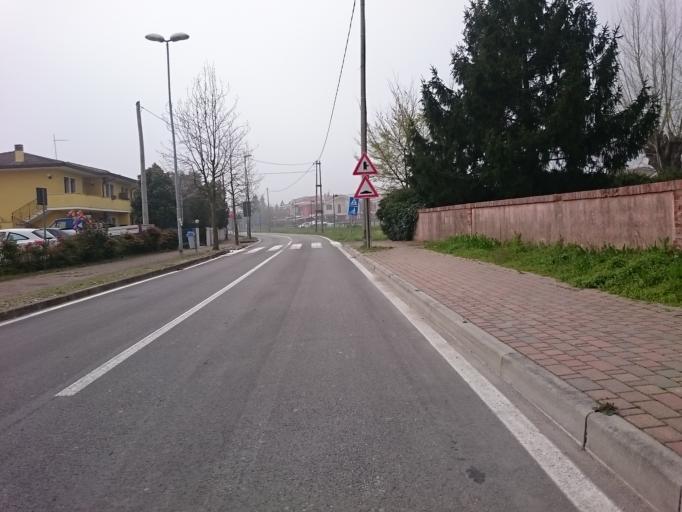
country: IT
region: Veneto
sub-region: Provincia di Padova
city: Masera di Padova
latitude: 45.3017
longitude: 11.8518
